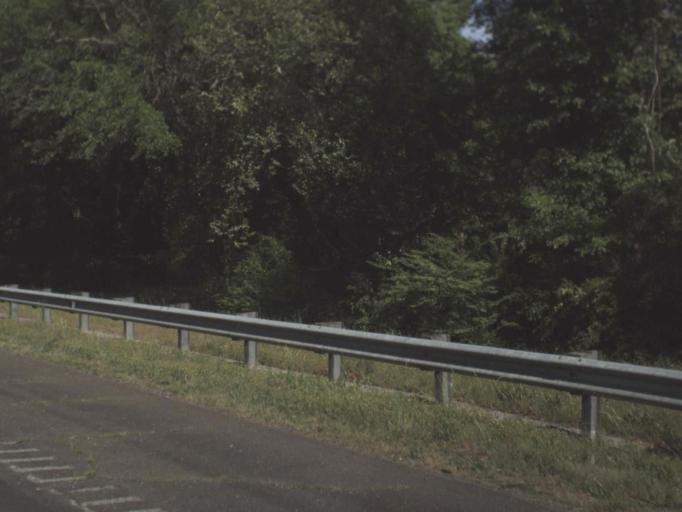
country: US
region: Florida
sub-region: Santa Rosa County
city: East Milton
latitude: 30.6365
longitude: -86.9181
